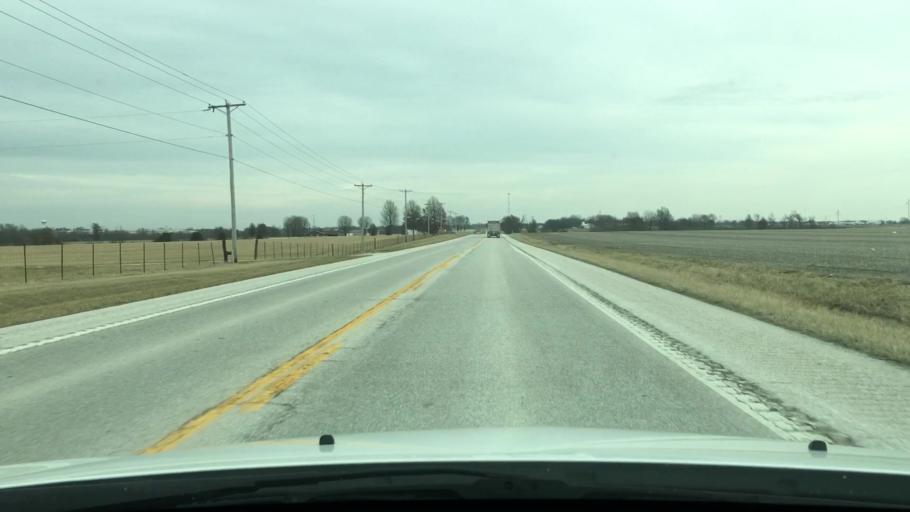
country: US
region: Missouri
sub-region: Pike County
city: Bowling Green
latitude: 39.3443
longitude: -91.2518
